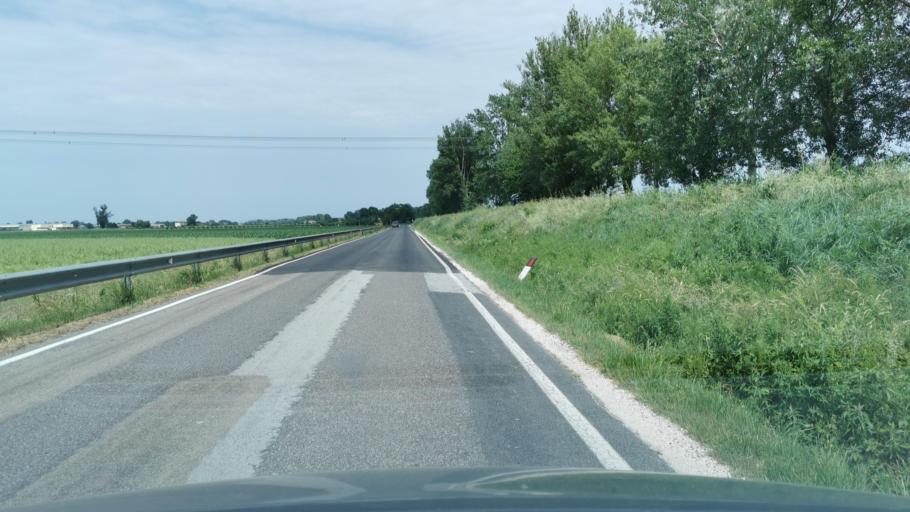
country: IT
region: Emilia-Romagna
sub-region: Provincia di Ravenna
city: Alfonsine
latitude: 44.4803
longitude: 12.0397
